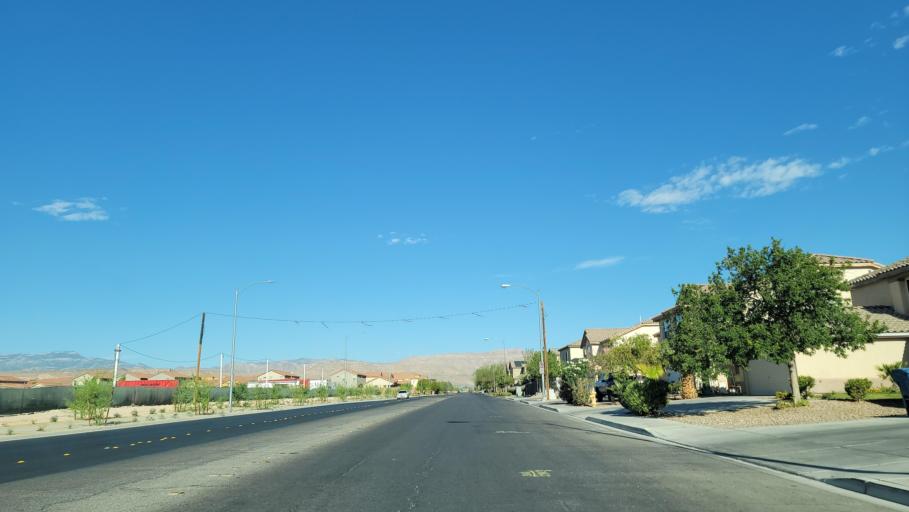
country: US
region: Nevada
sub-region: Clark County
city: Spring Valley
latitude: 36.0776
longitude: -115.2632
